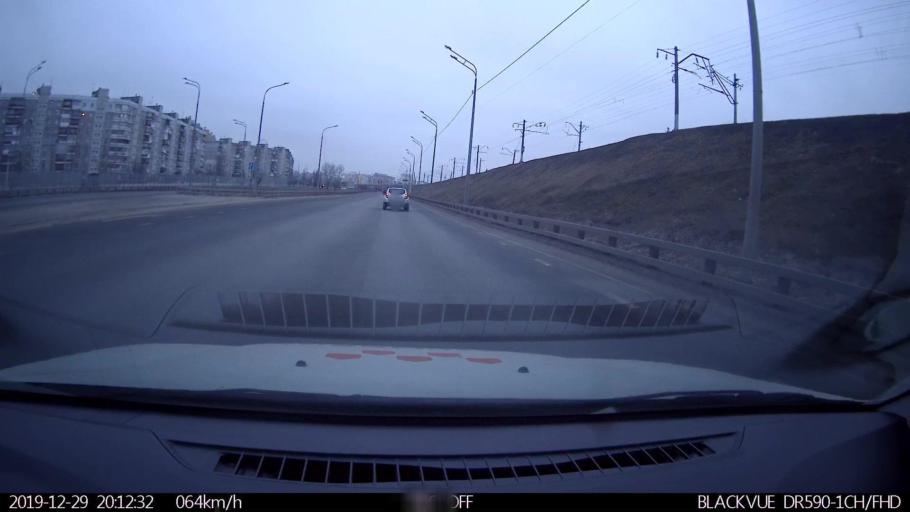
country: RU
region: Nizjnij Novgorod
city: Nizhniy Novgorod
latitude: 56.3453
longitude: 43.9217
